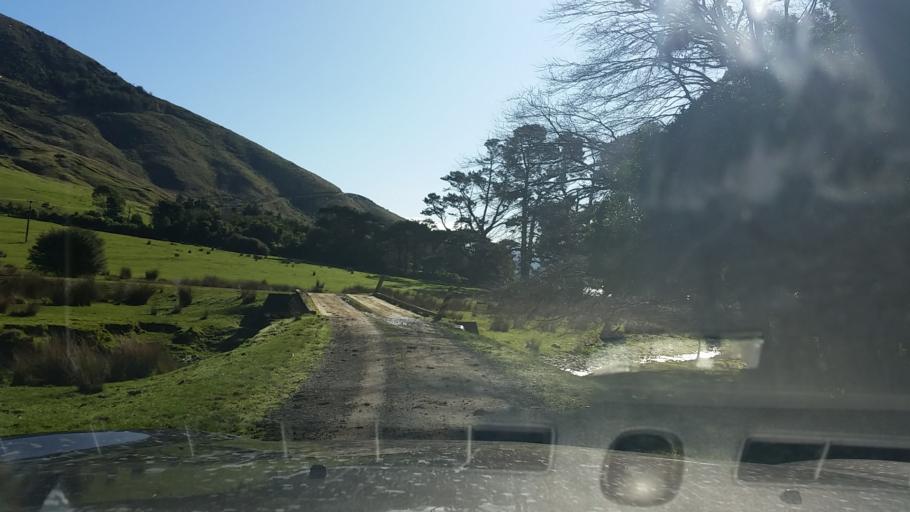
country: NZ
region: Marlborough
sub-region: Marlborough District
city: Picton
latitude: -41.1152
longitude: 174.0358
